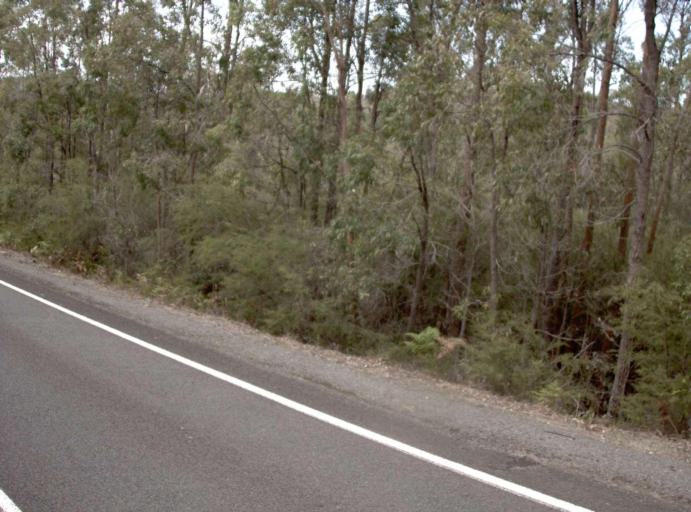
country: AU
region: New South Wales
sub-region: Bega Valley
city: Eden
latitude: -37.4905
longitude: 149.5505
